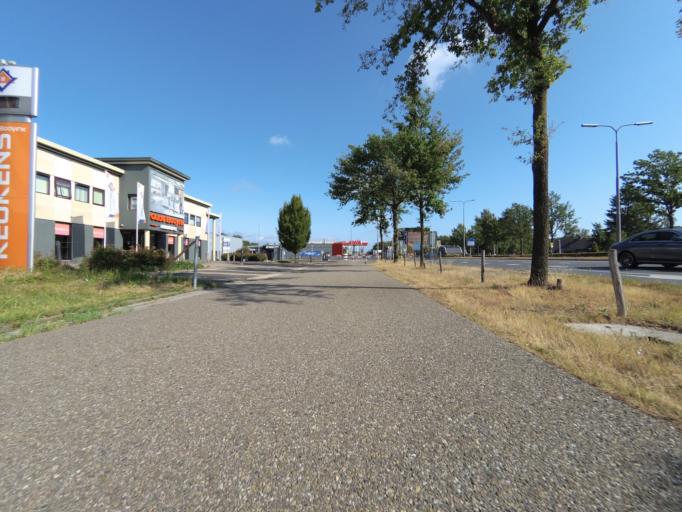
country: NL
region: Overijssel
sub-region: Gemeente Oldenzaal
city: Oldenzaal
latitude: 52.2899
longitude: 6.9298
